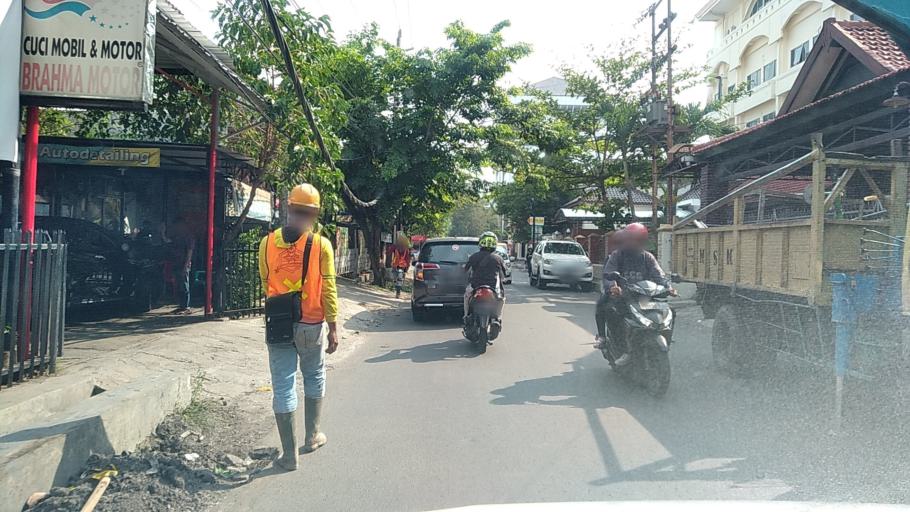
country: ID
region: Central Java
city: Semarang
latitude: -6.9924
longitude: 110.4231
